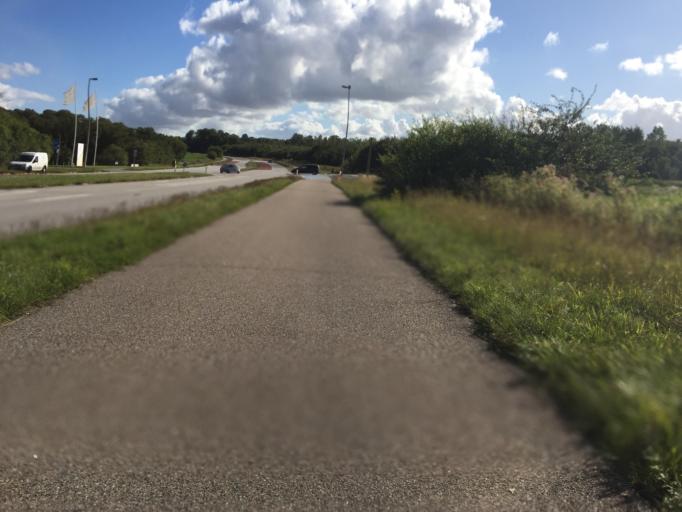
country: DK
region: Capital Region
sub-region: Fureso Kommune
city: Vaerlose
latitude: 55.7802
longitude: 12.4031
